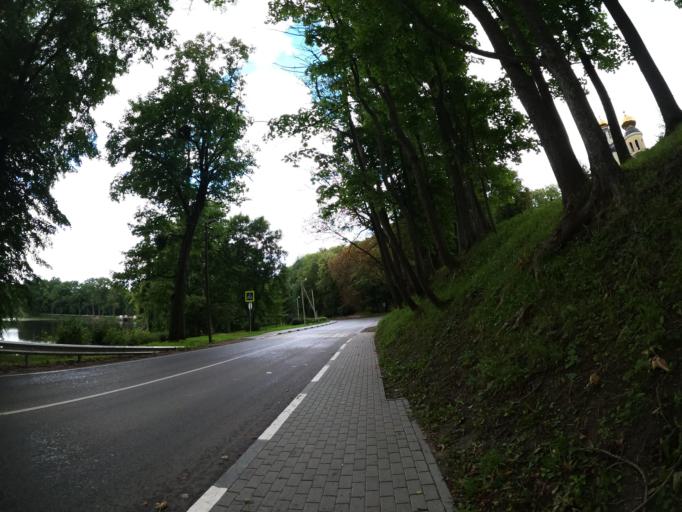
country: RU
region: Kaliningrad
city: Zheleznodorozhnyy
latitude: 54.3627
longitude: 21.3108
